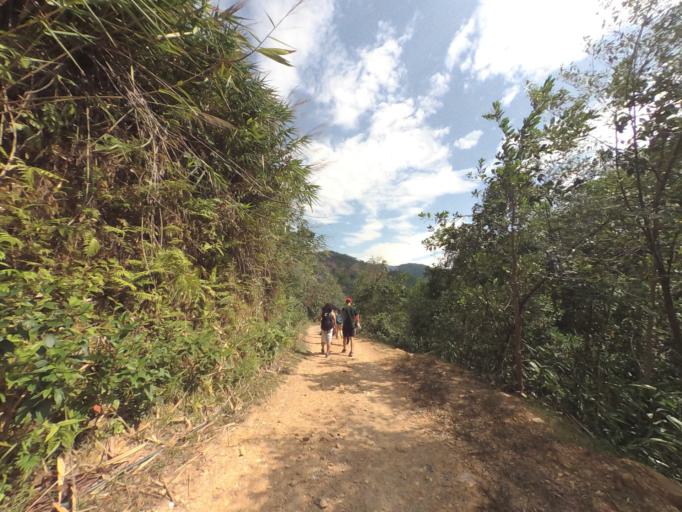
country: VN
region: Thua Thien-Hue
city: A Luoi
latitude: 16.3035
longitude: 107.3250
